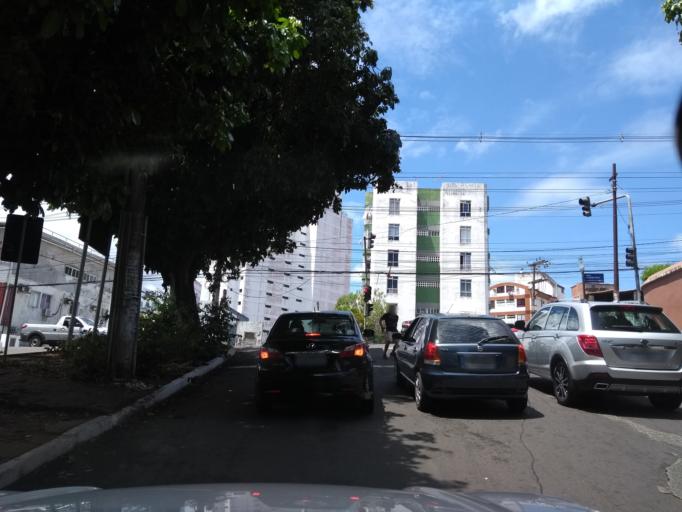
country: BR
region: Bahia
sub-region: Salvador
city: Salvador
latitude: -12.9973
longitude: -38.5159
